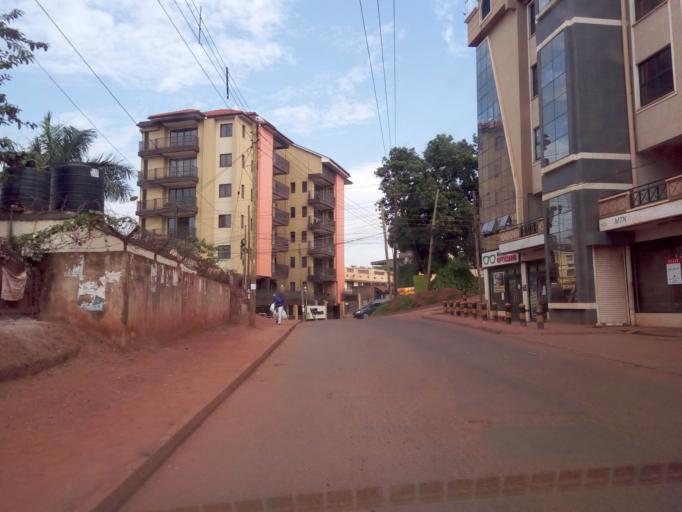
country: UG
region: Central Region
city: Kampala Central Division
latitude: 0.3397
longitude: 32.5845
